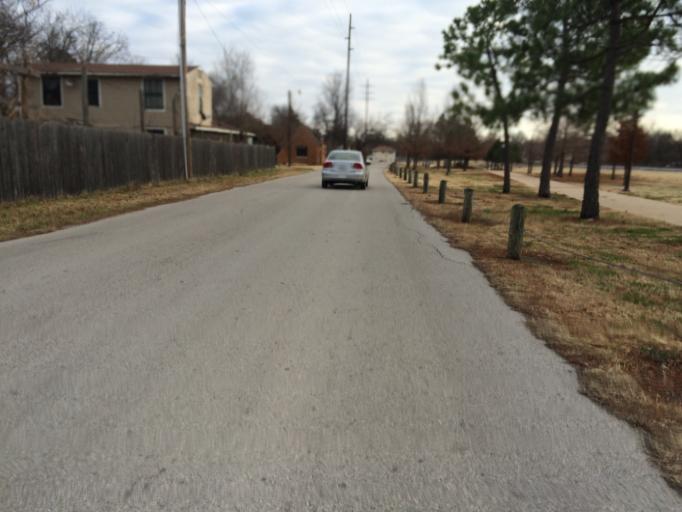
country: US
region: Oklahoma
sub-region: Cleveland County
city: Norman
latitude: 35.2164
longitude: -97.4404
